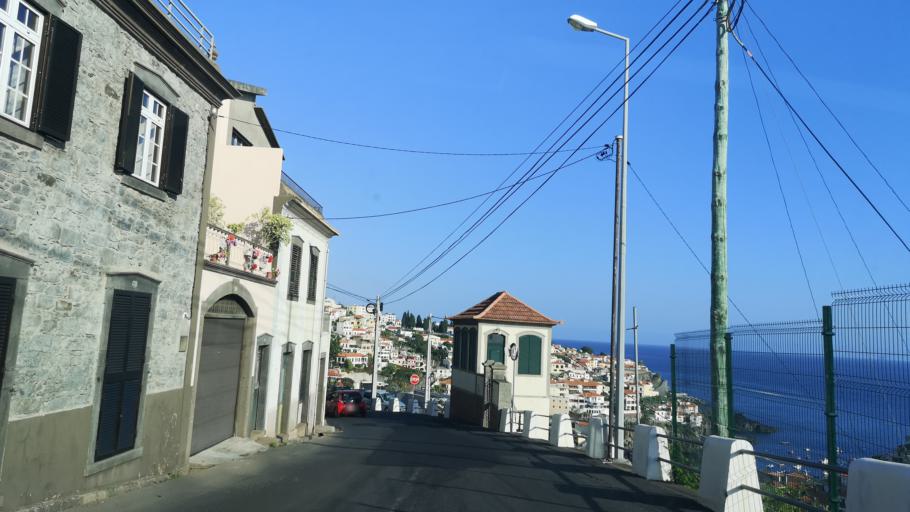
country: PT
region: Madeira
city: Camara de Lobos
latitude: 32.6502
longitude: -16.9776
